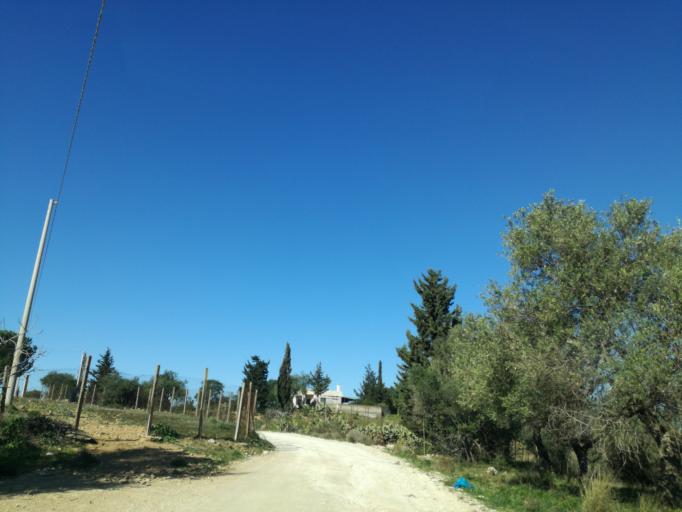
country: IT
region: Sicily
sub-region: Provincia di Caltanissetta
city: Niscemi
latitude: 37.0571
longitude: 14.3605
